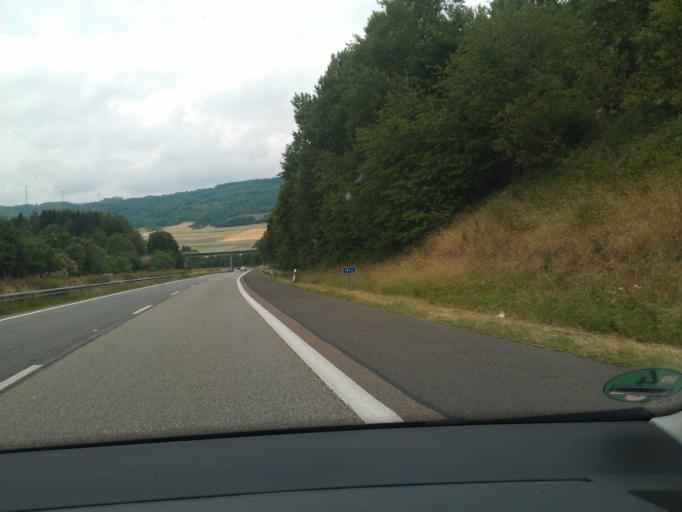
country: DE
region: Rheinland-Pfalz
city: Pfeffelbach
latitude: 49.5304
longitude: 7.3203
